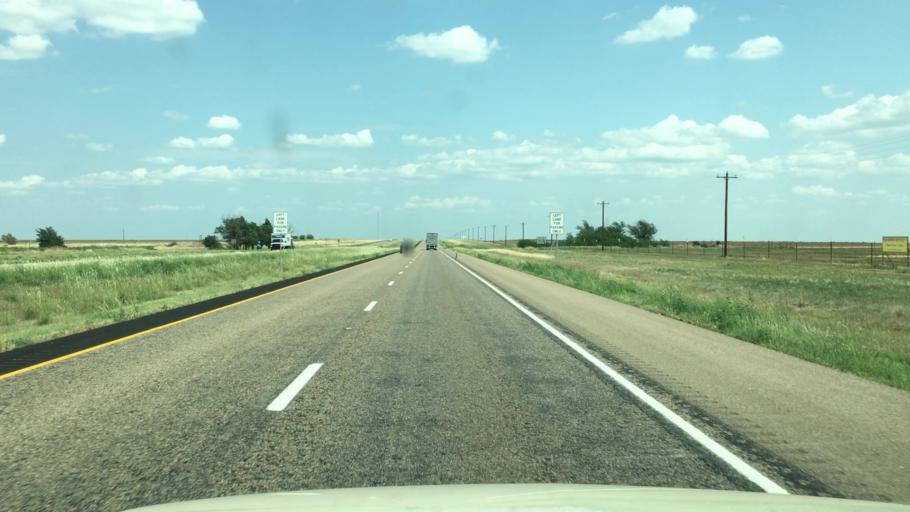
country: US
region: Texas
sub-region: Armstrong County
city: Claude
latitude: 35.0337
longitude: -101.1794
